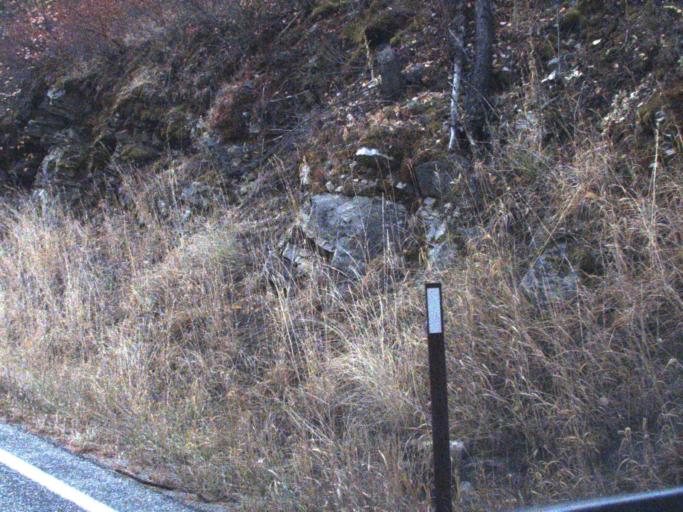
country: CA
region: British Columbia
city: Grand Forks
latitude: 48.8697
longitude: -118.2102
